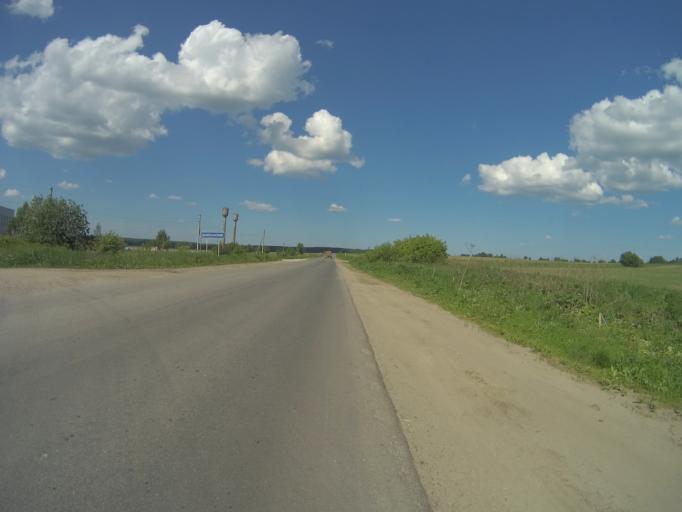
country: RU
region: Vladimir
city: Orgtrud
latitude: 56.2369
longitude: 40.5737
